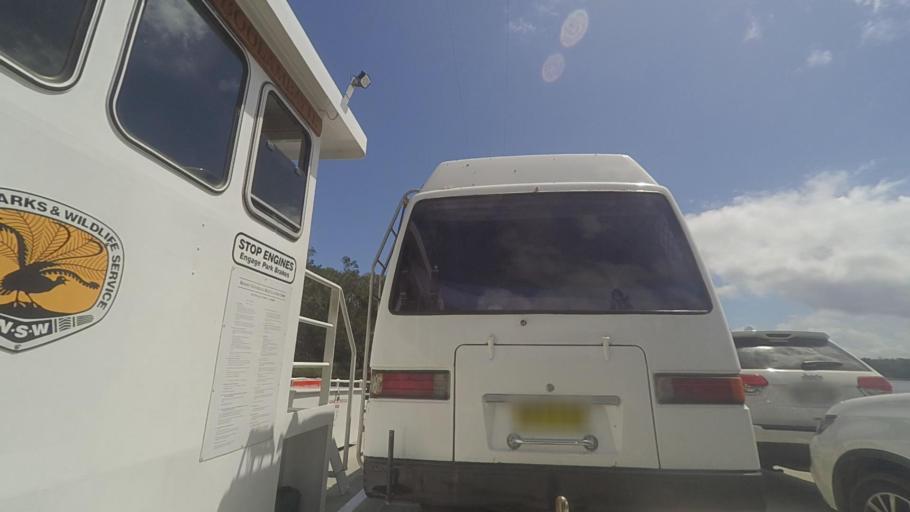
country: AU
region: New South Wales
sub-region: Great Lakes
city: Bulahdelah
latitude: -32.5044
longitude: 152.3046
